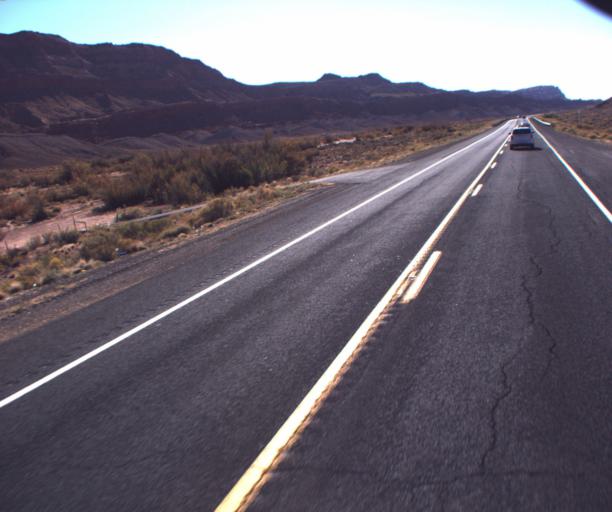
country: US
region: Arizona
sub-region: Coconino County
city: Tuba City
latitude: 36.2231
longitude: -111.3992
